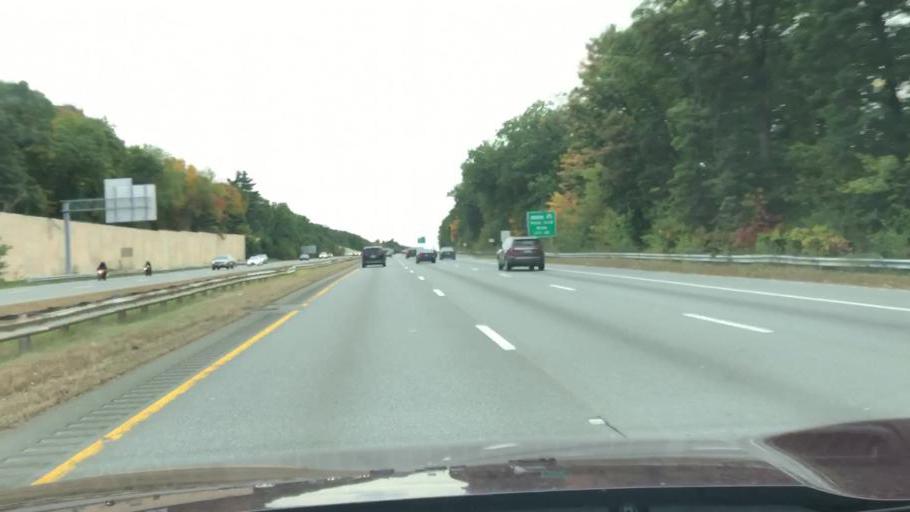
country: US
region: Massachusetts
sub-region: Essex County
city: Andover
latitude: 42.6377
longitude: -71.1824
